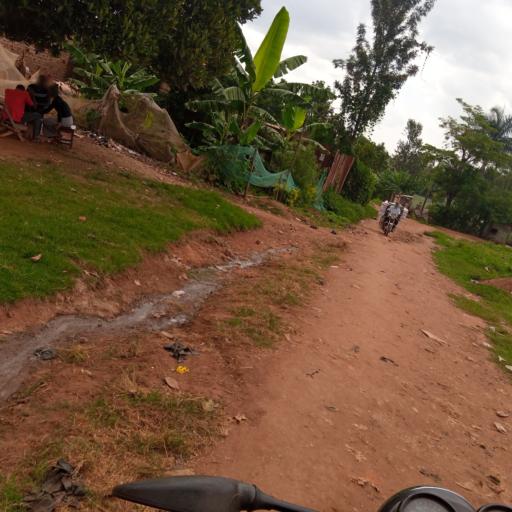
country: UG
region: Eastern Region
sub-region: Mbale District
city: Mbale
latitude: 1.0997
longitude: 34.1762
